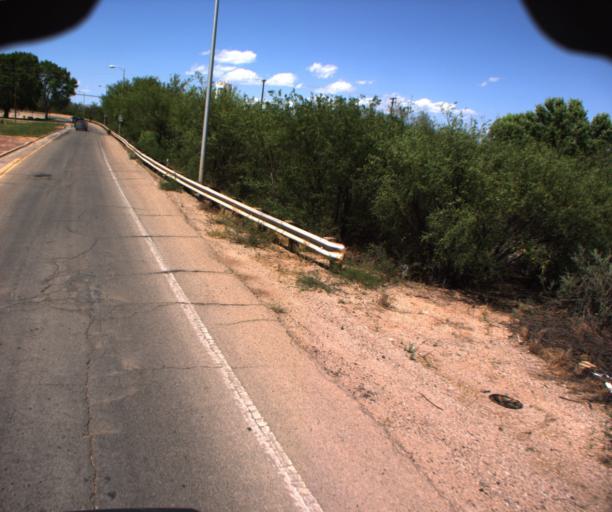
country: US
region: Arizona
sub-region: Cochise County
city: Benson
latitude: 31.9645
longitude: -110.2894
